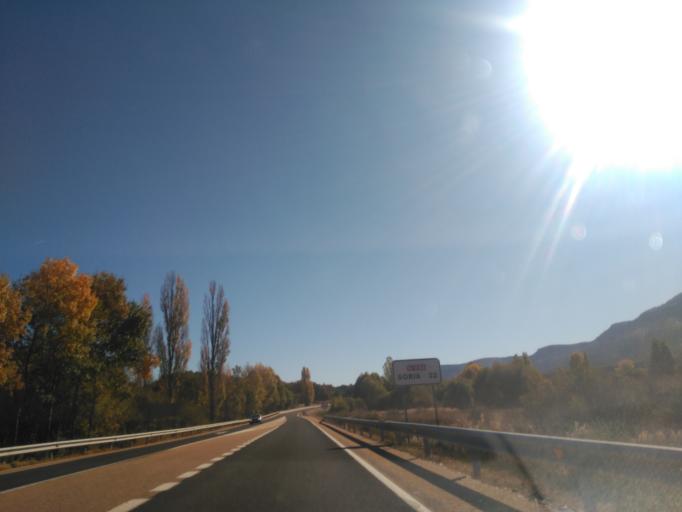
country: ES
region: Castille and Leon
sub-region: Provincia de Soria
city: Abejar
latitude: 41.8136
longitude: -2.7129
